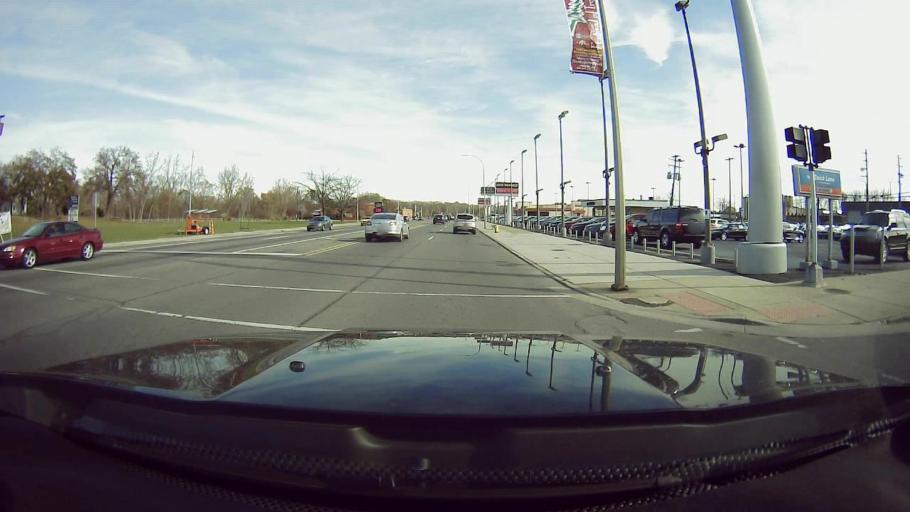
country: US
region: Michigan
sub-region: Wayne County
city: Dearborn Heights
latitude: 42.3071
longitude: -83.2401
